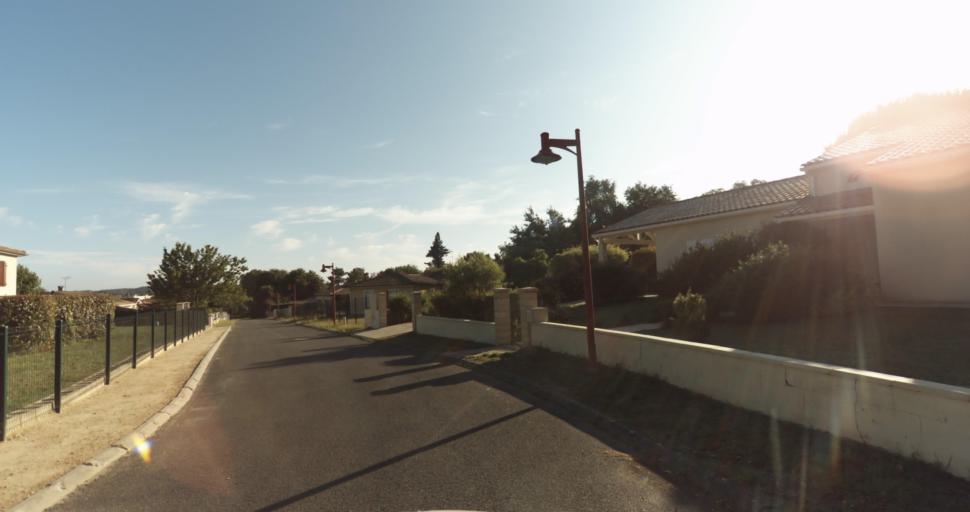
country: FR
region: Aquitaine
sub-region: Departement de la Gironde
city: Bazas
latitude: 44.4262
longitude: -0.2166
